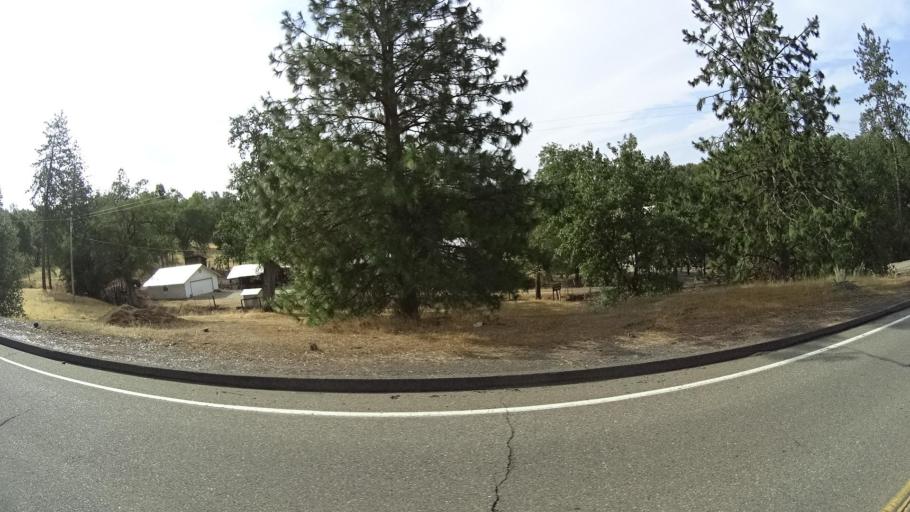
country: US
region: California
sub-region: Madera County
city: Ahwahnee
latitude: 37.4633
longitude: -119.7742
